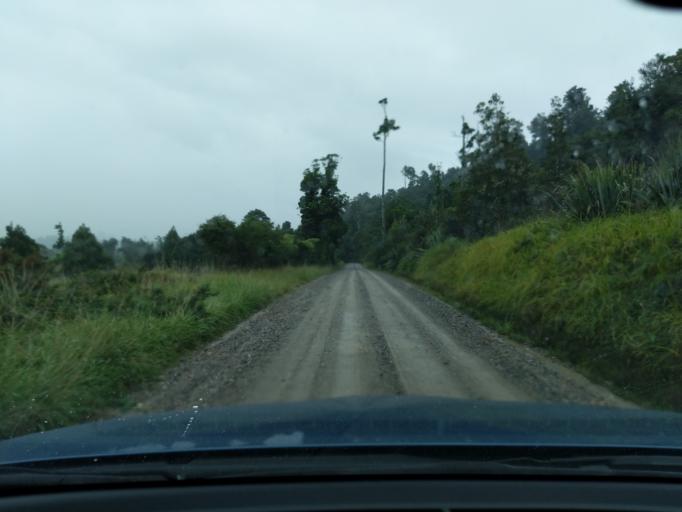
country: NZ
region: Tasman
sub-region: Tasman District
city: Takaka
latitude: -40.6469
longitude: 172.4717
